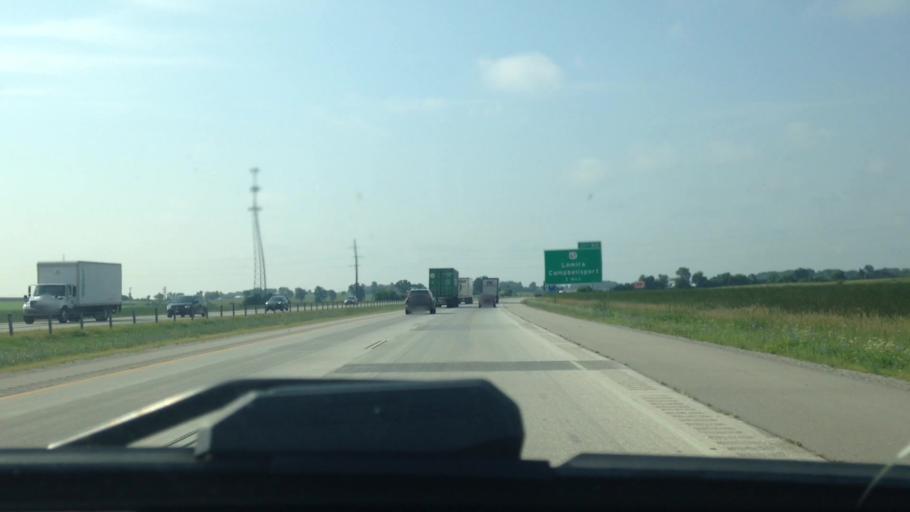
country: US
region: Wisconsin
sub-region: Dodge County
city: Lomira
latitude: 43.6049
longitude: -88.4319
